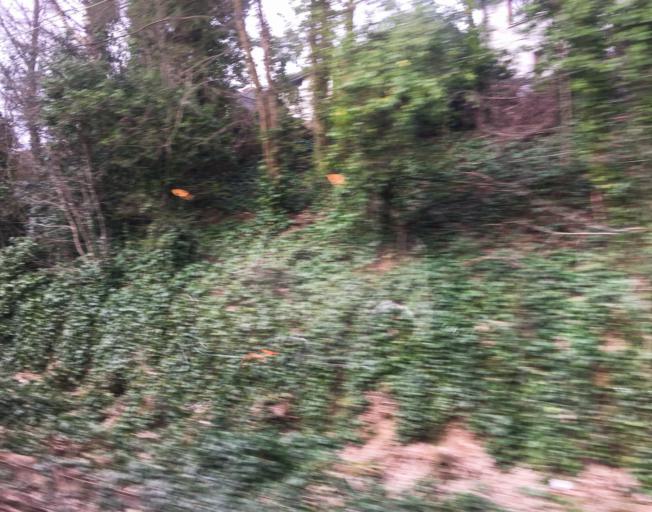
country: GB
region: Scotland
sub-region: East Dunbartonshire
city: Bearsden
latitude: 55.9047
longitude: -4.3590
